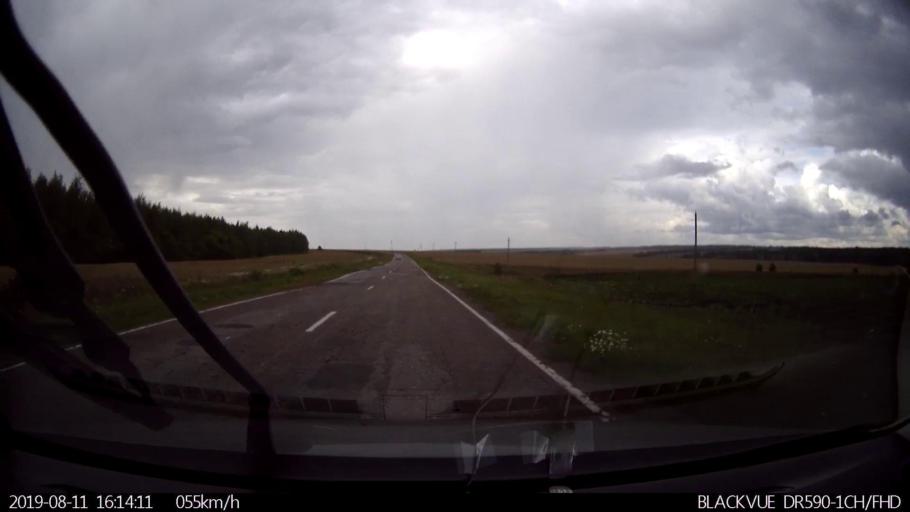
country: RU
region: Ulyanovsk
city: Ignatovka
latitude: 54.0260
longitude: 47.6347
